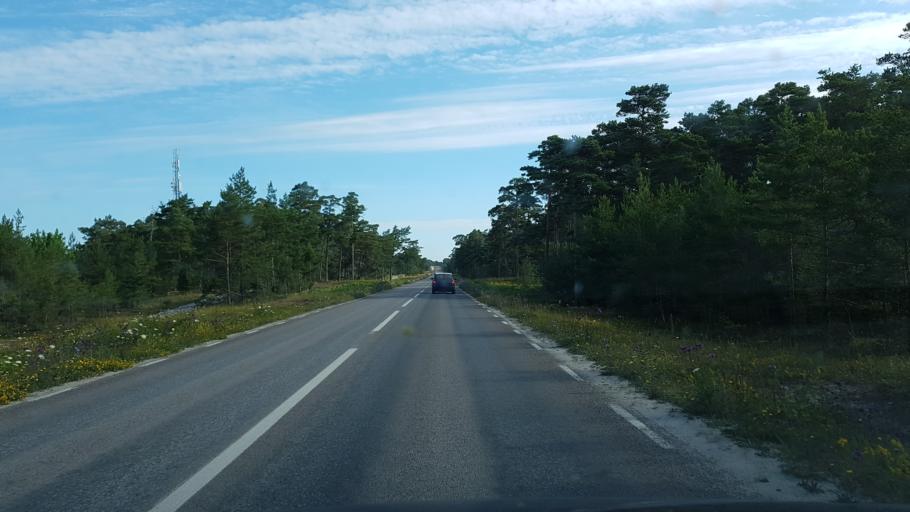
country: SE
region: Gotland
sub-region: Gotland
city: Visby
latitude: 57.6963
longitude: 18.3770
